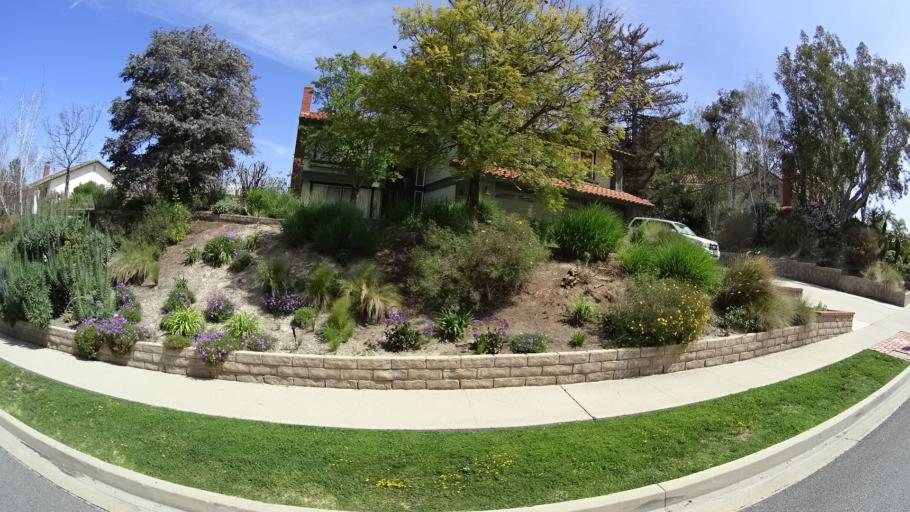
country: US
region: California
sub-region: Ventura County
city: Thousand Oaks
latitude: 34.2255
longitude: -118.8367
